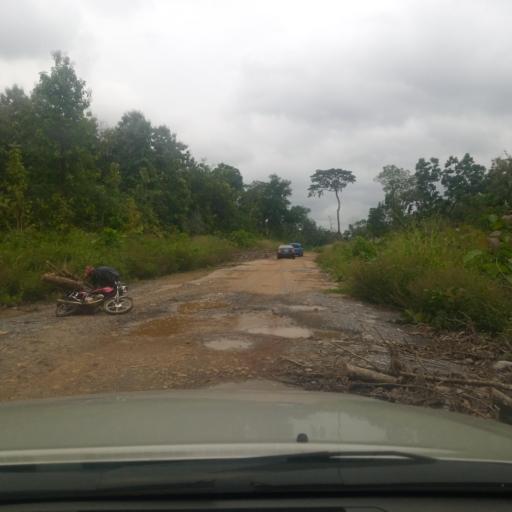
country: NG
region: Ebonyi
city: Effium
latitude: 6.6245
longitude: 8.0482
